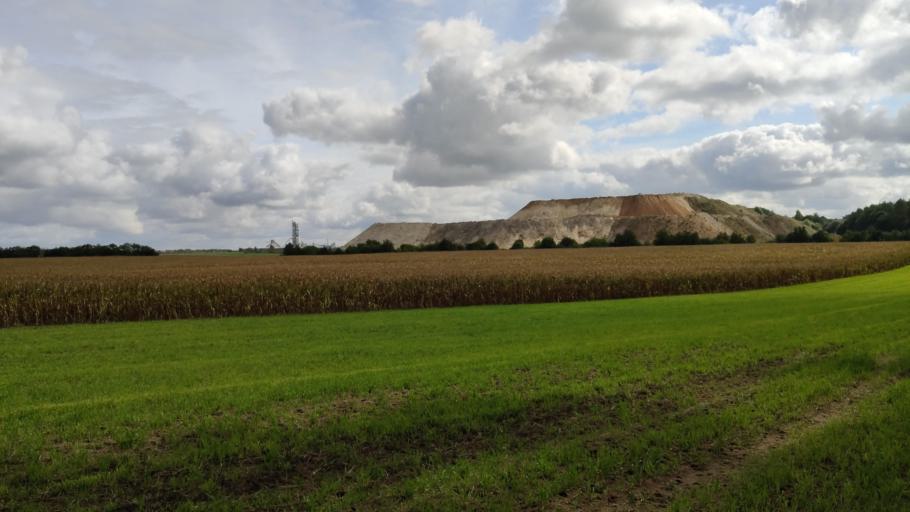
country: PL
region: Kujawsko-Pomorskie
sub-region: Powiat zninski
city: Barcin
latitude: 52.8350
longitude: 17.9457
